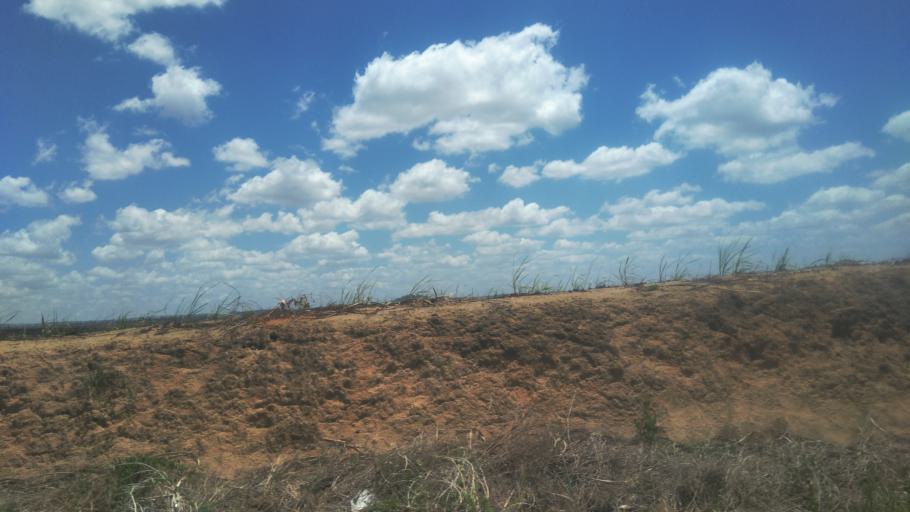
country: BR
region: Pernambuco
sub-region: Nazare Da Mata
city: Nazare da Mata
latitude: -7.7324
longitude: -35.2509
